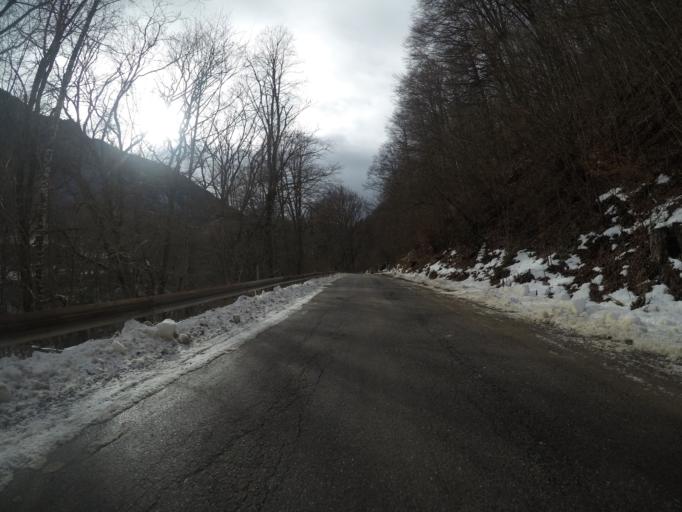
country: BG
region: Kyustendil
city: Sapareva Banya
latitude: 42.1382
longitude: 23.3455
